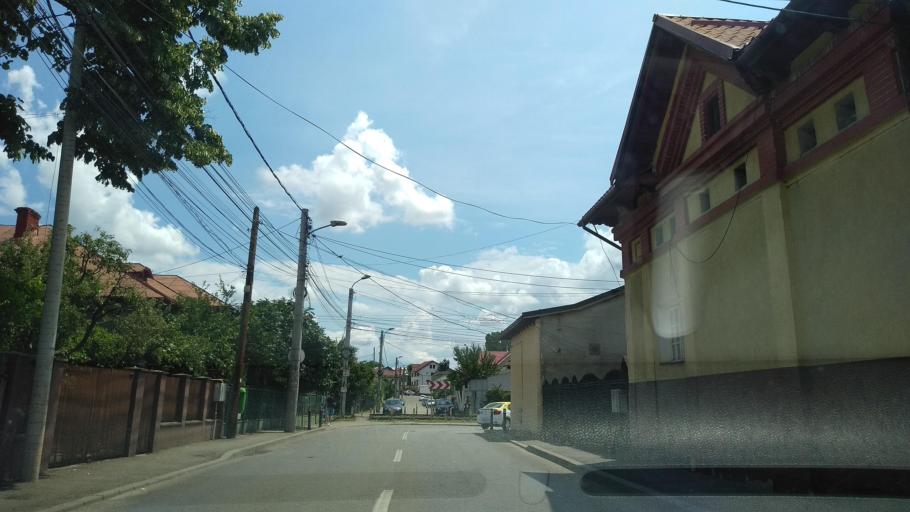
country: RO
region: Gorj
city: Targu Jiu
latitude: 45.0370
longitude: 23.2801
